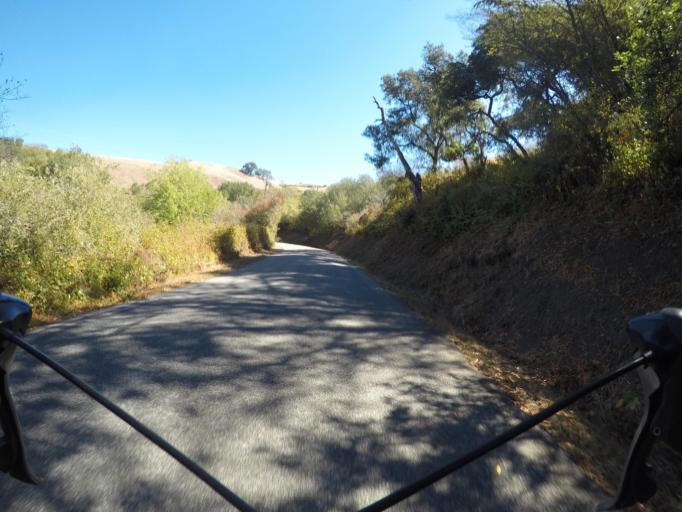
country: US
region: California
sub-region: San Mateo County
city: Portola Valley
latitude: 37.3596
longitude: -122.2538
